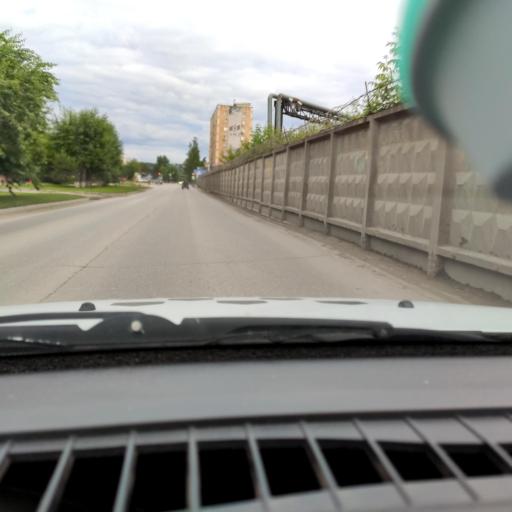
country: RU
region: Perm
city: Chusovoy
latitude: 58.2967
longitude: 57.8117
